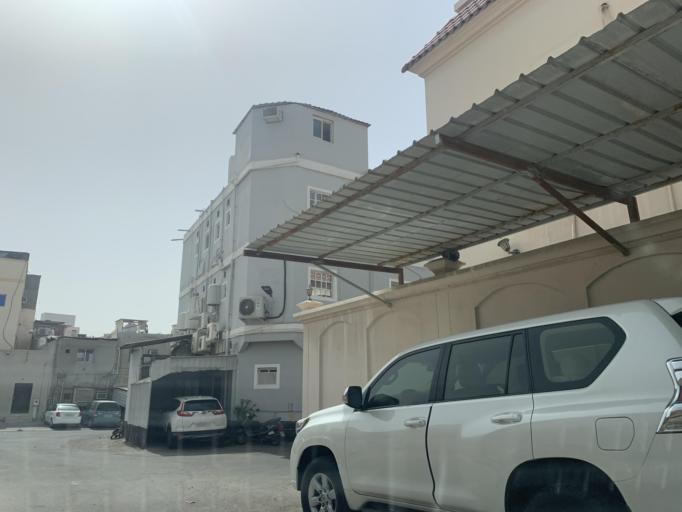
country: BH
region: Northern
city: Madinat `Isa
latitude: 26.1566
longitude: 50.5150
